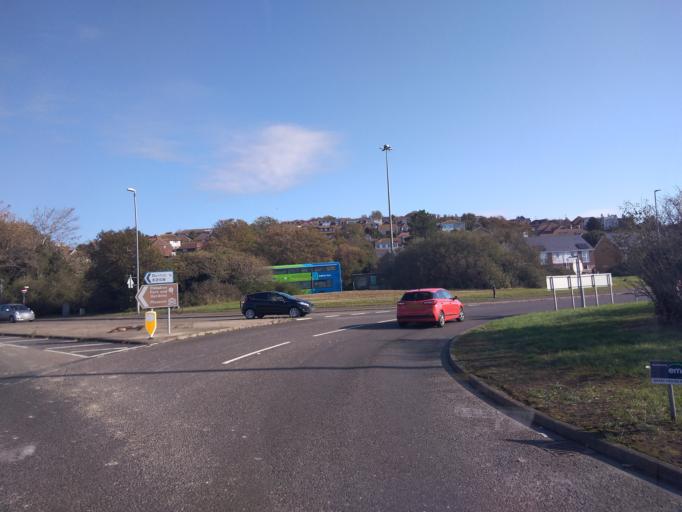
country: GB
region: England
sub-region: East Sussex
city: Newhaven
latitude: 50.7986
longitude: 0.0625
